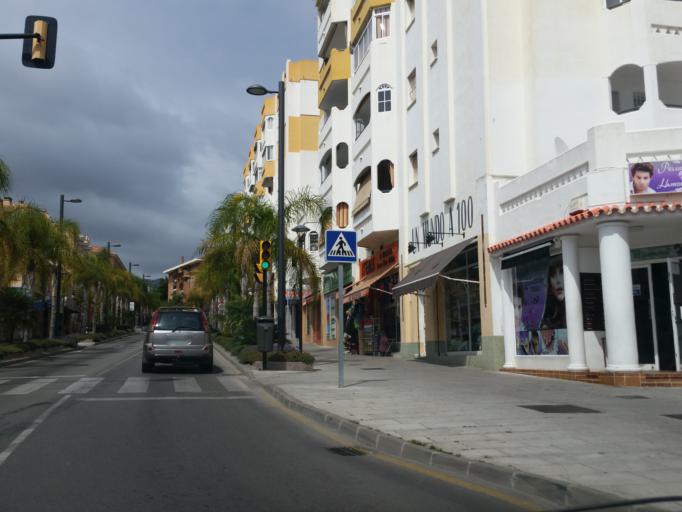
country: ES
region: Andalusia
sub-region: Provincia de Malaga
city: Benalmadena
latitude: 36.5970
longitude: -4.5313
